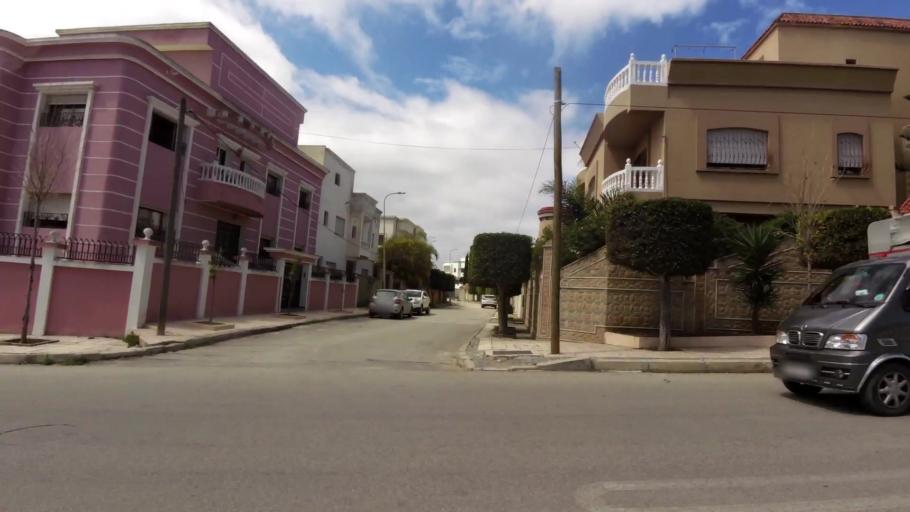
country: MA
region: Tanger-Tetouan
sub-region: Tanger-Assilah
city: Tangier
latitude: 35.7654
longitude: -5.8398
